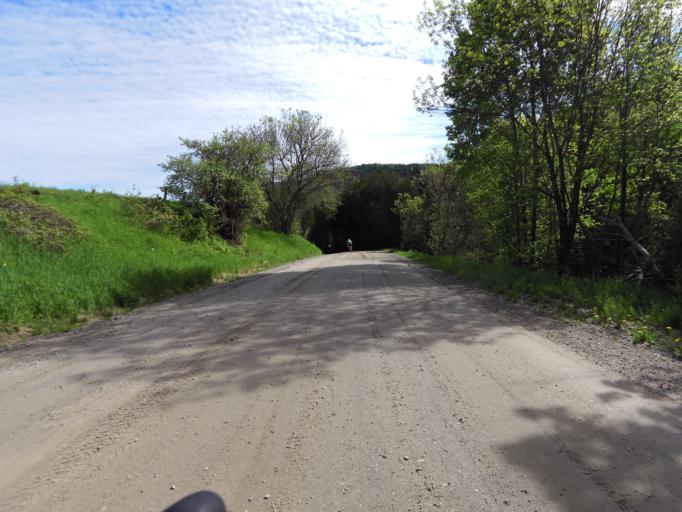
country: CA
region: Quebec
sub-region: Outaouais
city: Wakefield
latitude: 45.6914
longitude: -75.8889
